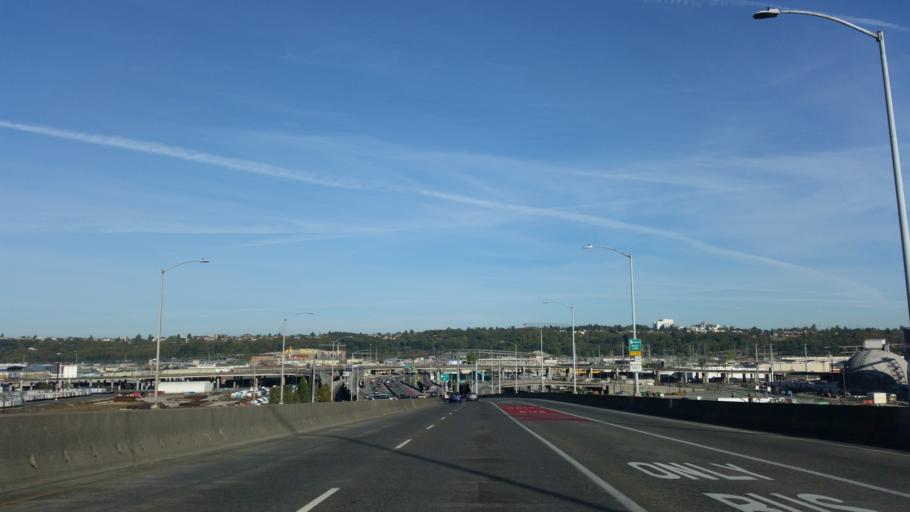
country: US
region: Washington
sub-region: King County
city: Seattle
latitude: 47.5710
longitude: -122.3483
